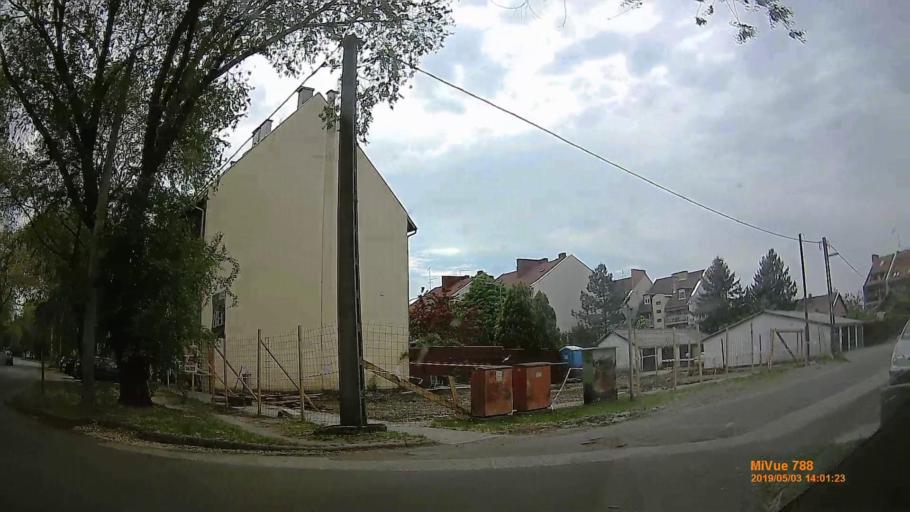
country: HU
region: Jasz-Nagykun-Szolnok
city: Szolnok
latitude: 47.1853
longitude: 20.1933
